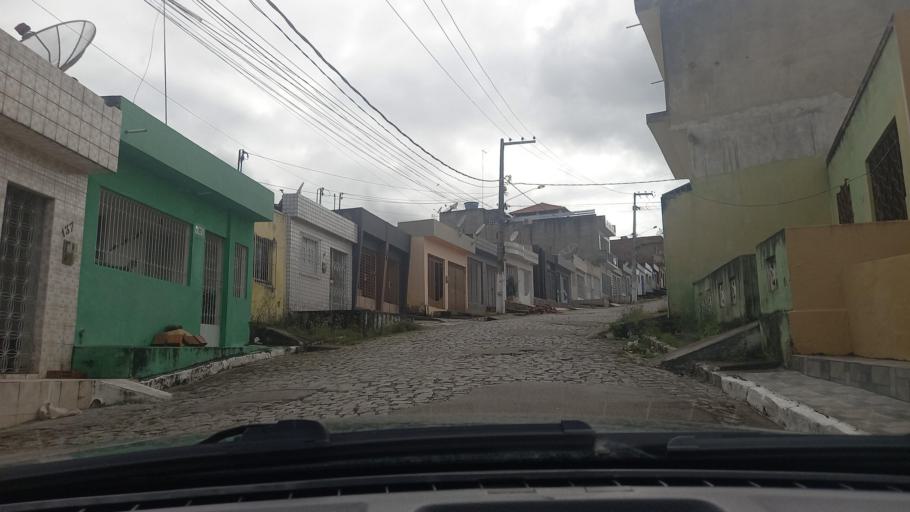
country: BR
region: Pernambuco
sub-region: Vitoria De Santo Antao
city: Vitoria de Santo Antao
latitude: -8.1115
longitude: -35.3005
